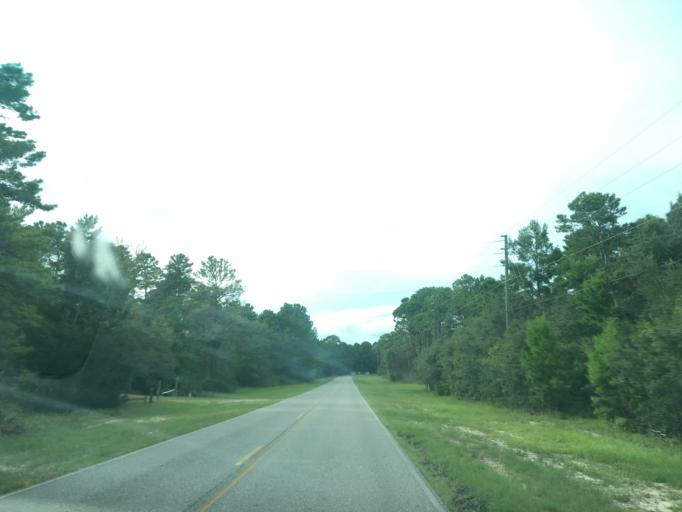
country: US
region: Florida
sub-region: Wakulla County
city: Crawfordville
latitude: 29.9262
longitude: -84.3764
